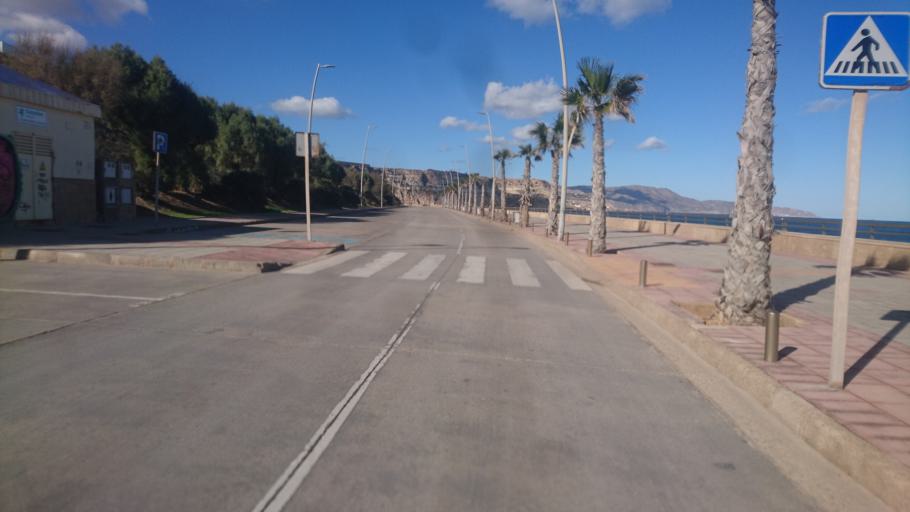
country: ES
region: Melilla
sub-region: Melilla
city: Melilla
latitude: 35.3023
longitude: -2.9376
